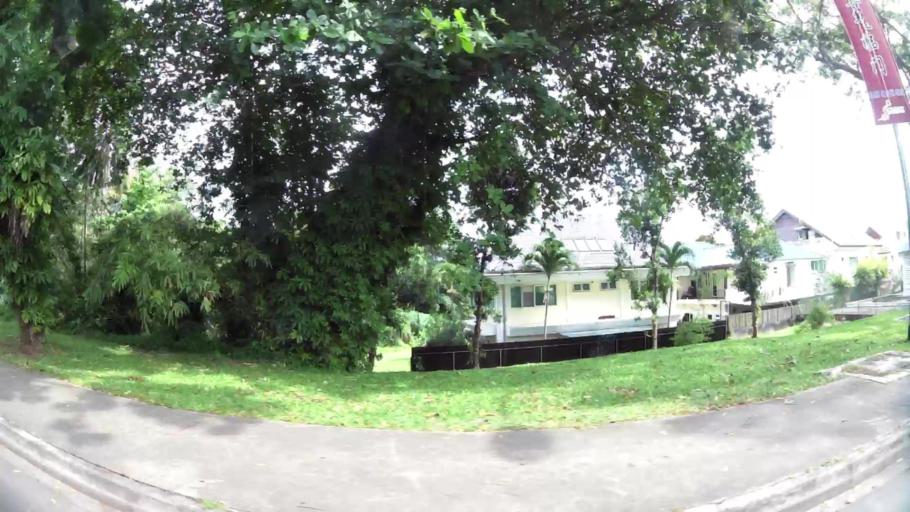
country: SG
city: Singapore
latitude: 1.3635
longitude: 103.9699
